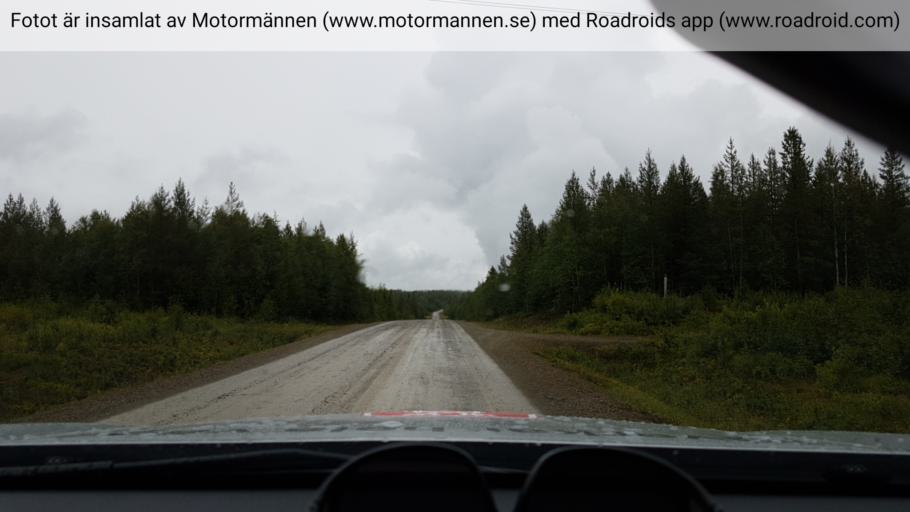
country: SE
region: Vaesterbotten
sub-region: Asele Kommun
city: Insjon
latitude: 64.8000
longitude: 17.5823
